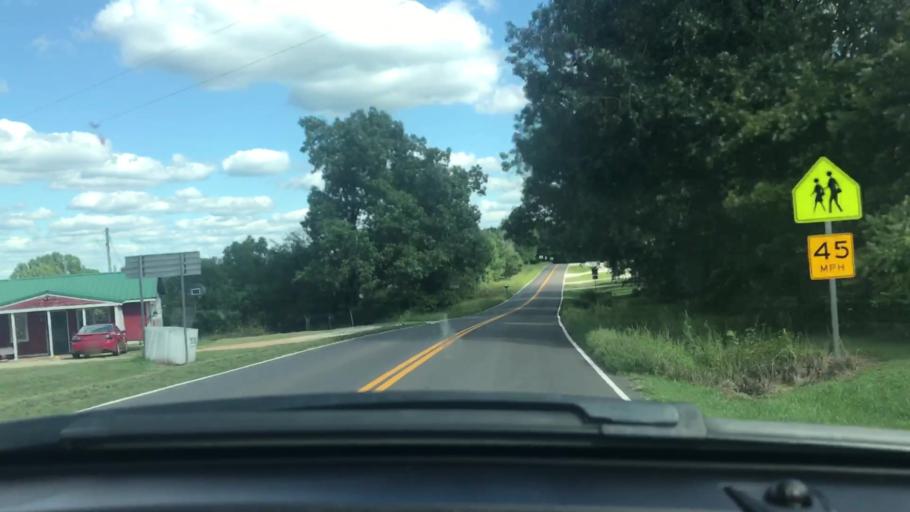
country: US
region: Missouri
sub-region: Wright County
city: Hartville
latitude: 37.3795
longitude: -92.3615
